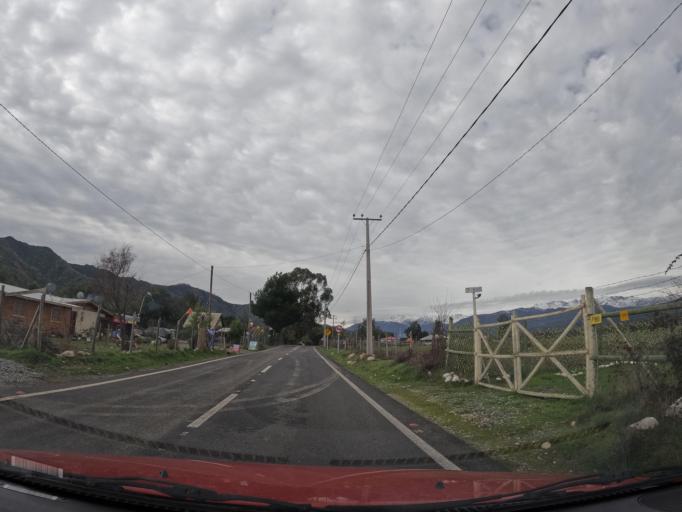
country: CL
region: Maule
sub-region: Provincia de Linares
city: Linares
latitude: -35.9247
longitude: -71.4170
